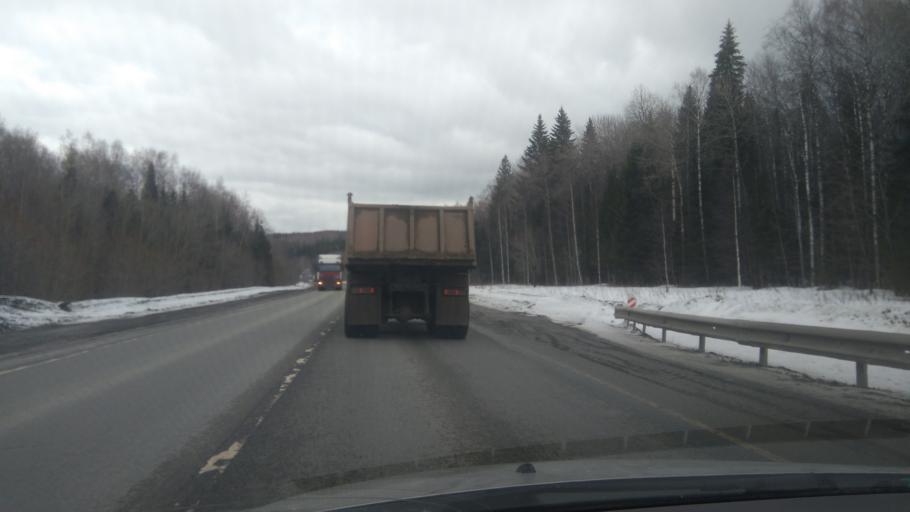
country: RU
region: Sverdlovsk
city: Bisert'
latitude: 56.8285
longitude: 59.0974
